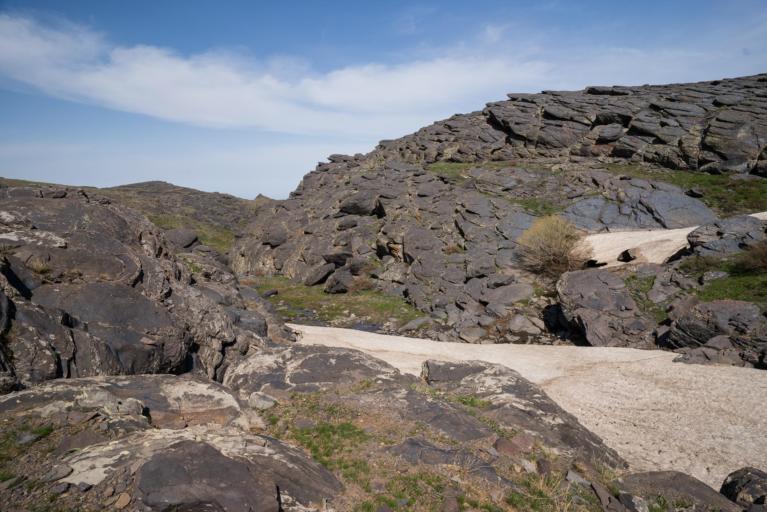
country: KZ
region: Ongtustik Qazaqstan
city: Kentau
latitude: 43.8405
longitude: 68.4843
